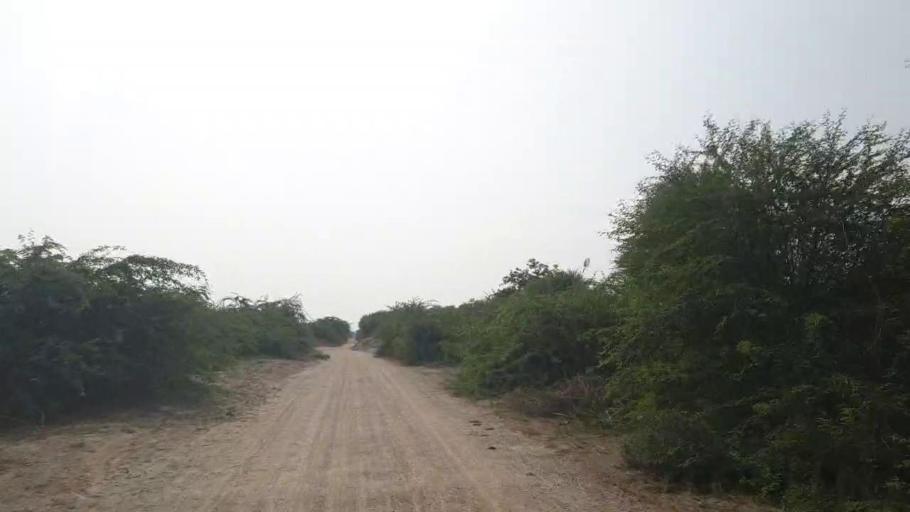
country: PK
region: Sindh
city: Badin
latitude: 24.6094
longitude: 68.7210
